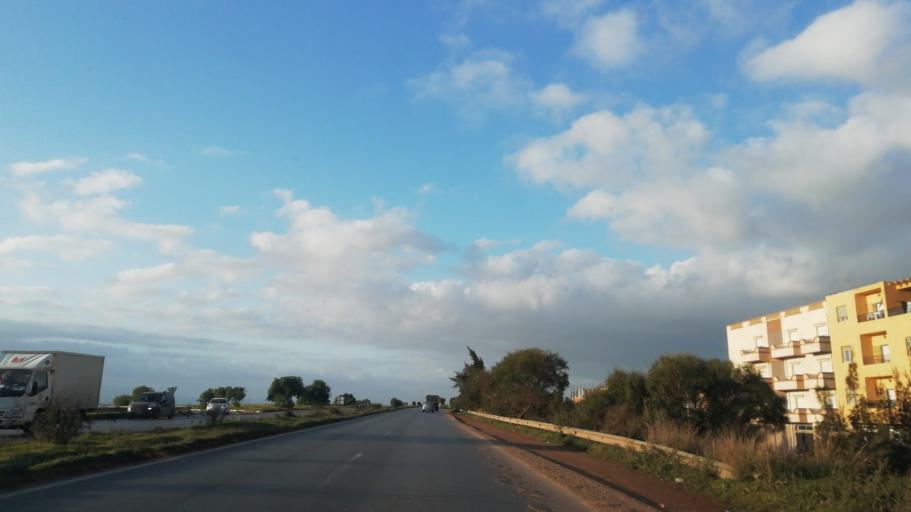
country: DZ
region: Oran
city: Es Senia
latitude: 35.6131
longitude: -0.7230
